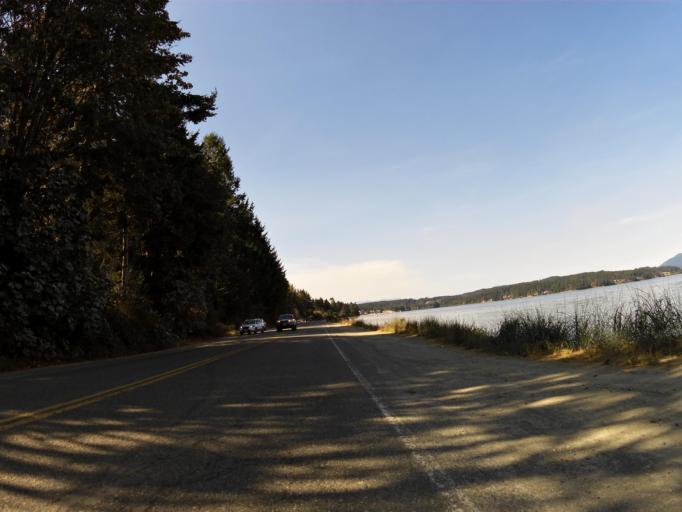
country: CA
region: British Columbia
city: North Saanich
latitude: 48.6339
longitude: -123.5327
